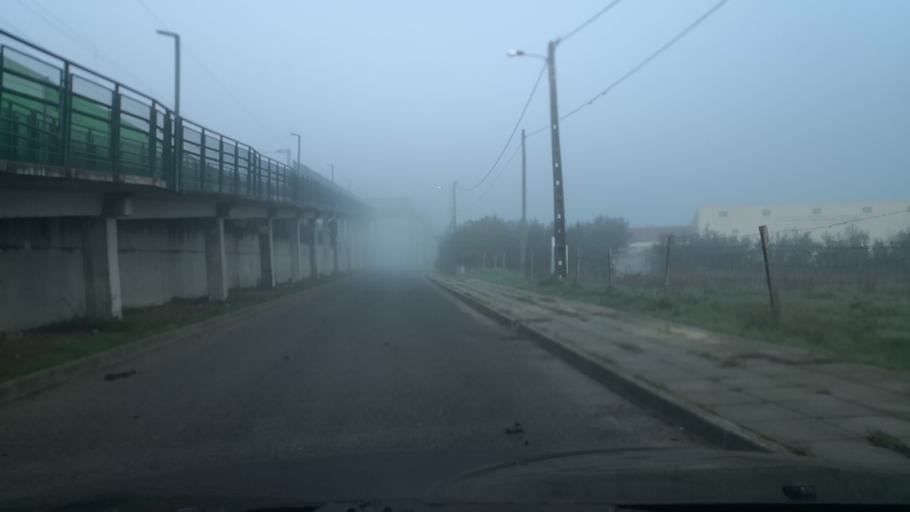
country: PT
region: Setubal
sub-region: Palmela
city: Pinhal Novo
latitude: 38.6079
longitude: -8.8896
